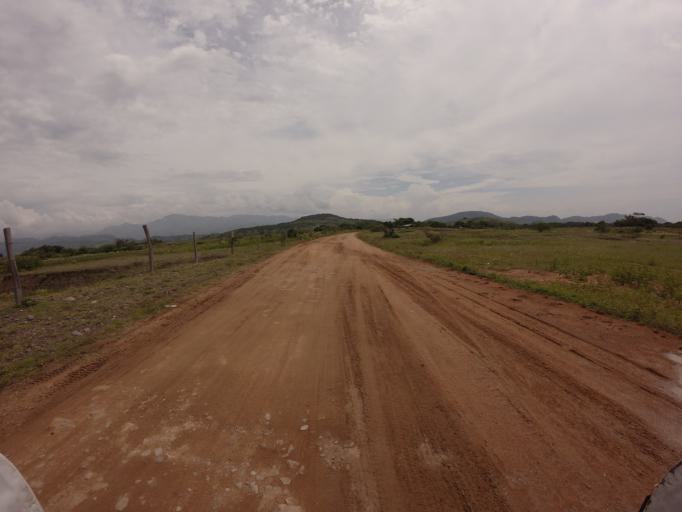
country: CO
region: Tolima
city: Natagaima
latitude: 3.4648
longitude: -75.1418
